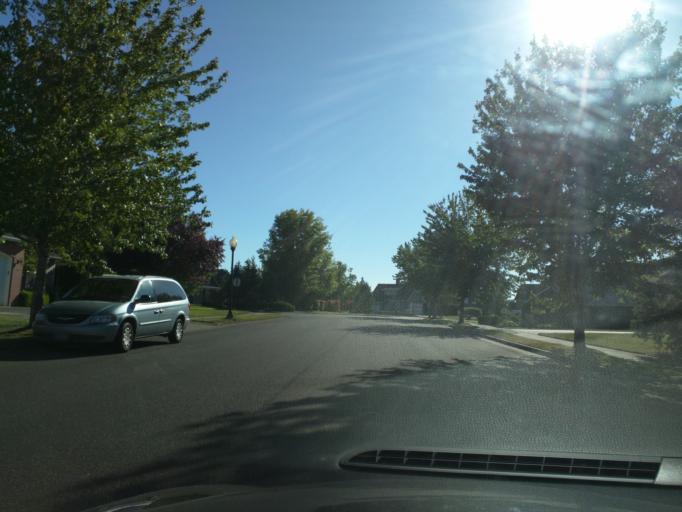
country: US
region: Washington
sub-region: Whatcom County
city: Lynden
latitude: 48.9570
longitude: -122.4594
